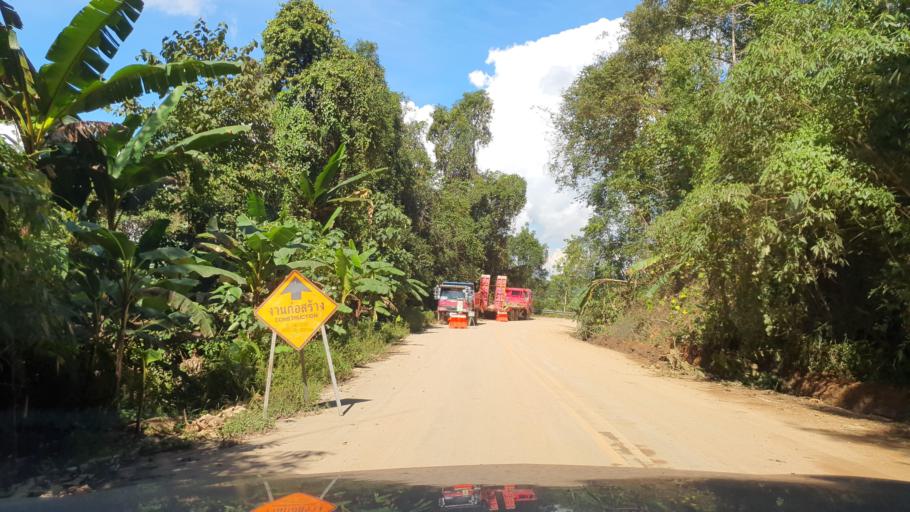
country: TH
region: Chiang Mai
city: Phrao
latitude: 19.3109
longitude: 99.3332
